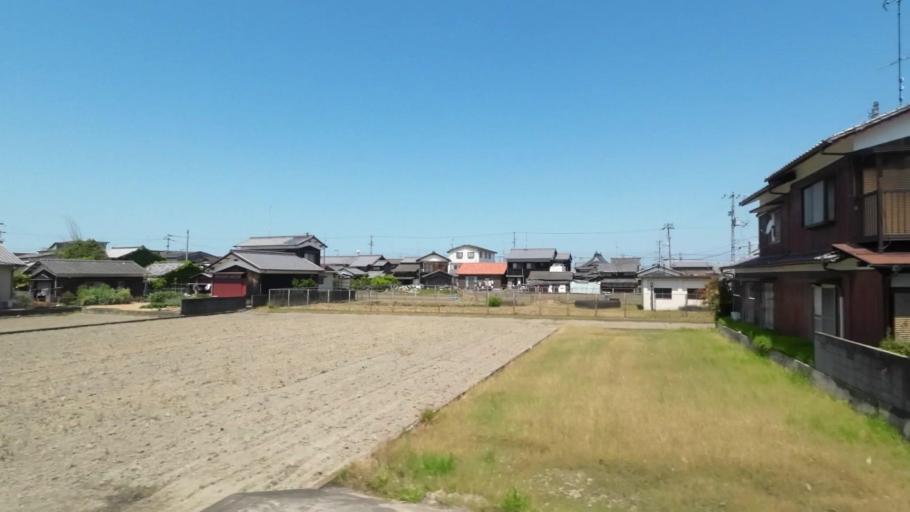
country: JP
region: Ehime
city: Hojo
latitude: 34.0363
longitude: 132.8456
